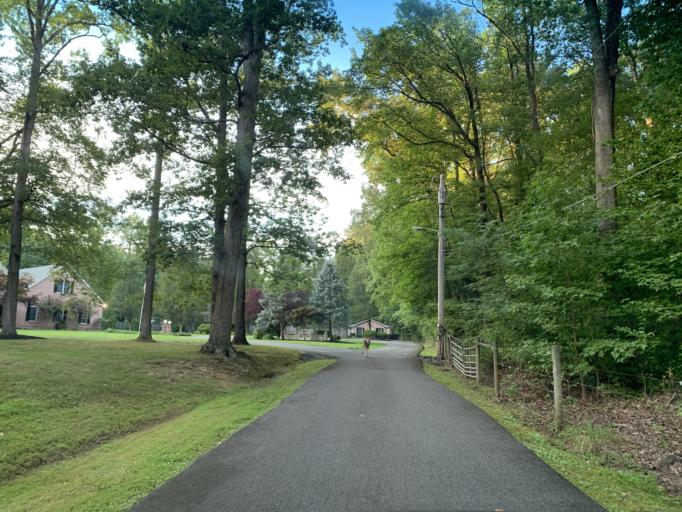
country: US
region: Maryland
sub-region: Harford County
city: Aberdeen
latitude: 39.5240
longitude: -76.1588
